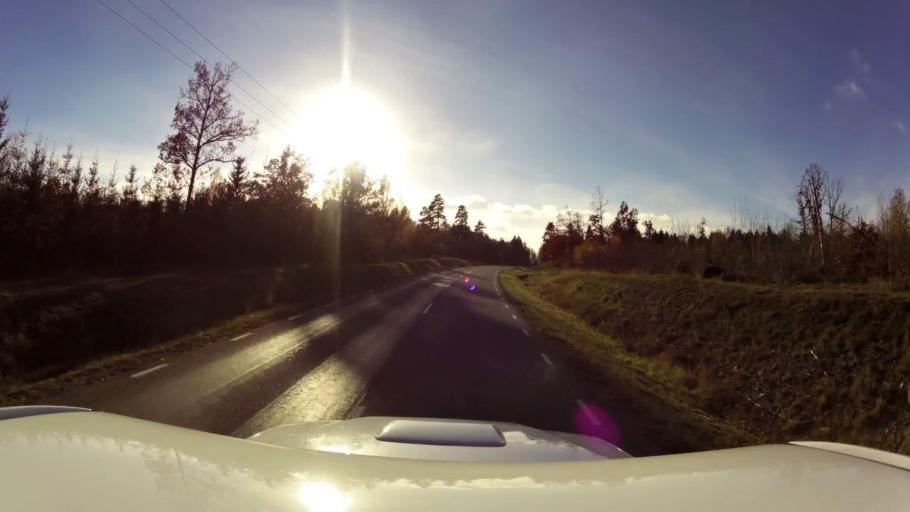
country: SE
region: OEstergoetland
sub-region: Linkopings Kommun
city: Vikingstad
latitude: 58.2949
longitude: 15.4657
